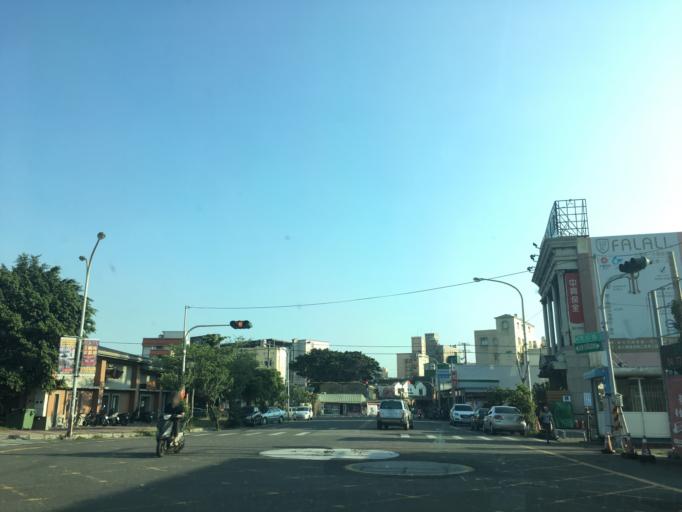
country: TW
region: Taiwan
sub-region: Changhua
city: Chang-hua
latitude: 24.0600
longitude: 120.4340
